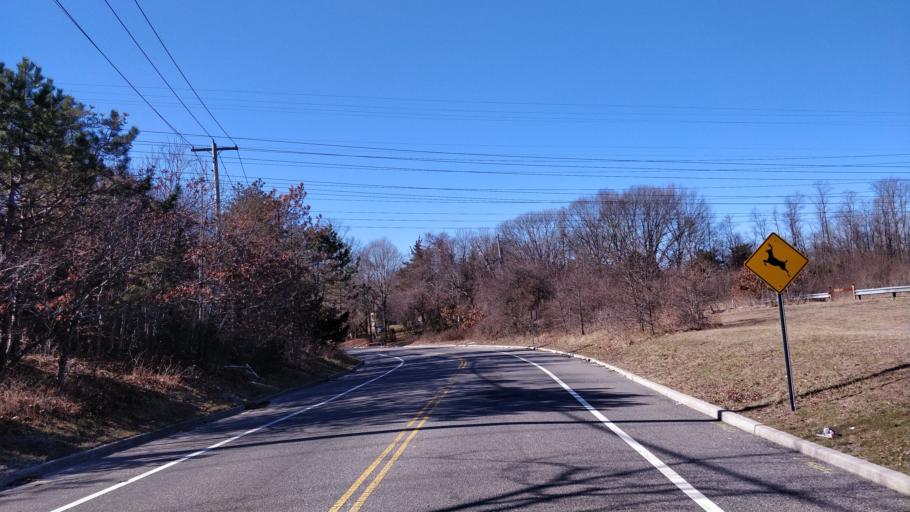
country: US
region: New York
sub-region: Suffolk County
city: Setauket-East Setauket
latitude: 40.9219
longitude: -73.0867
